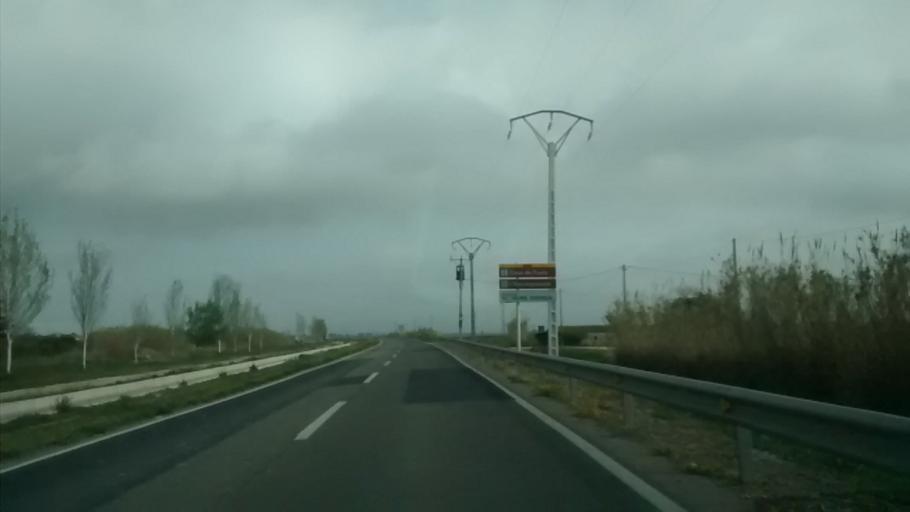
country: ES
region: Catalonia
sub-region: Provincia de Tarragona
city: Sant Carles de la Rapita
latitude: 40.6369
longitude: 0.6017
